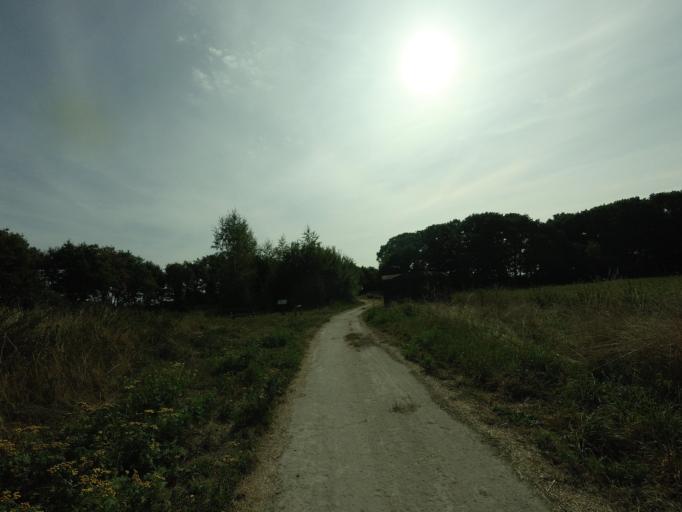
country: NL
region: North Brabant
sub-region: Gemeente Sint Anthonis
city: Sint Anthonis
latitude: 51.5816
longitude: 5.8415
